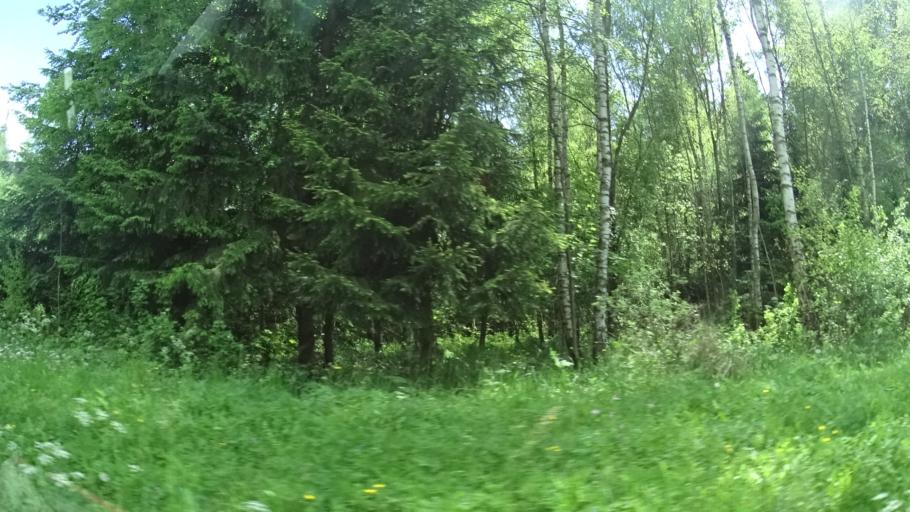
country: DE
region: Thuringia
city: Schmeheim
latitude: 50.5884
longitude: 10.5863
